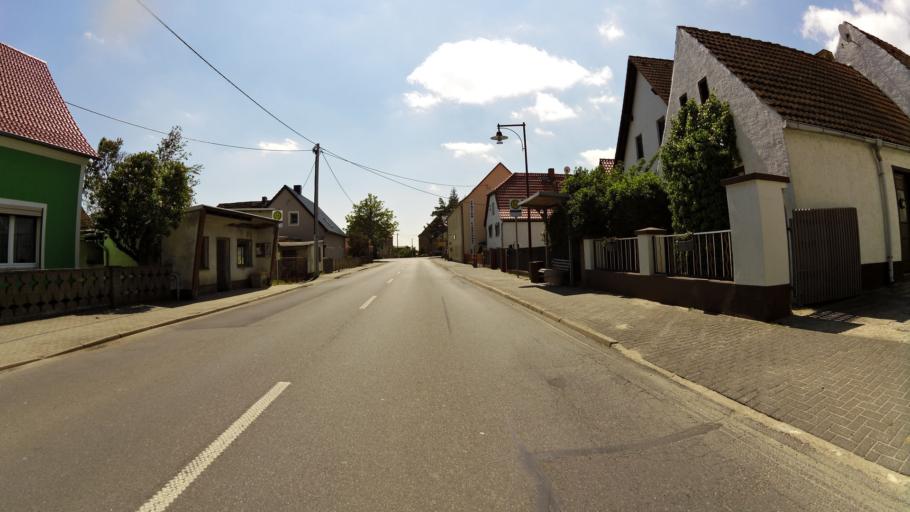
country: DE
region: Brandenburg
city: Muhlberg
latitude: 51.4456
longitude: 13.1724
